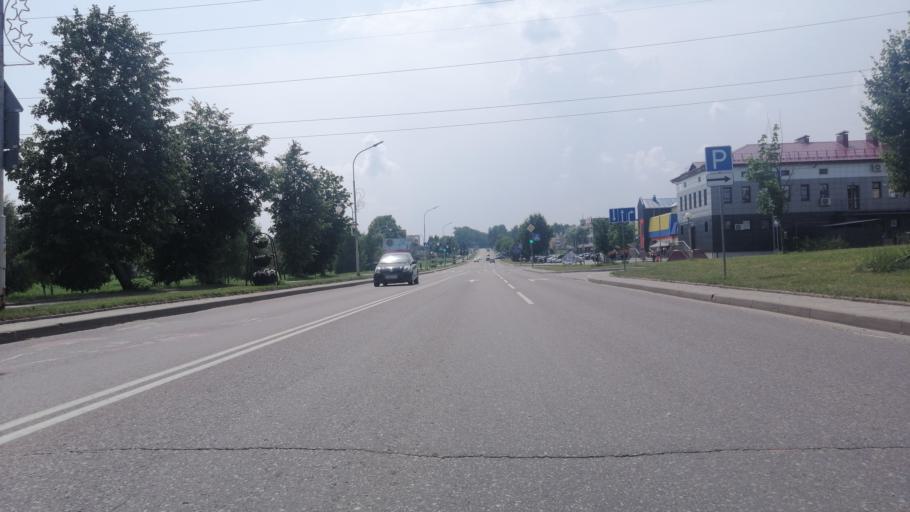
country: BY
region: Grodnenskaya
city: Navahrudak
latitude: 53.5857
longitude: 25.8082
